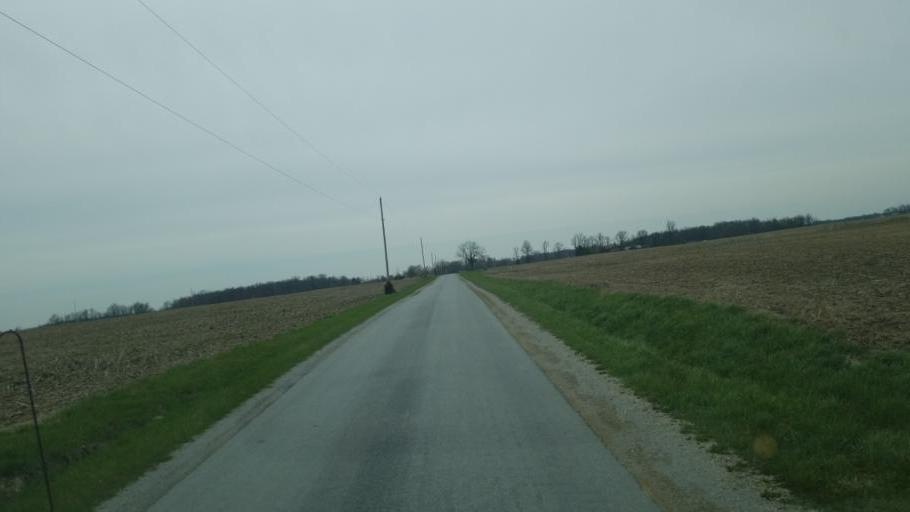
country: US
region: Ohio
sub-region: Hardin County
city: Forest
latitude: 40.8203
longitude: -83.4922
